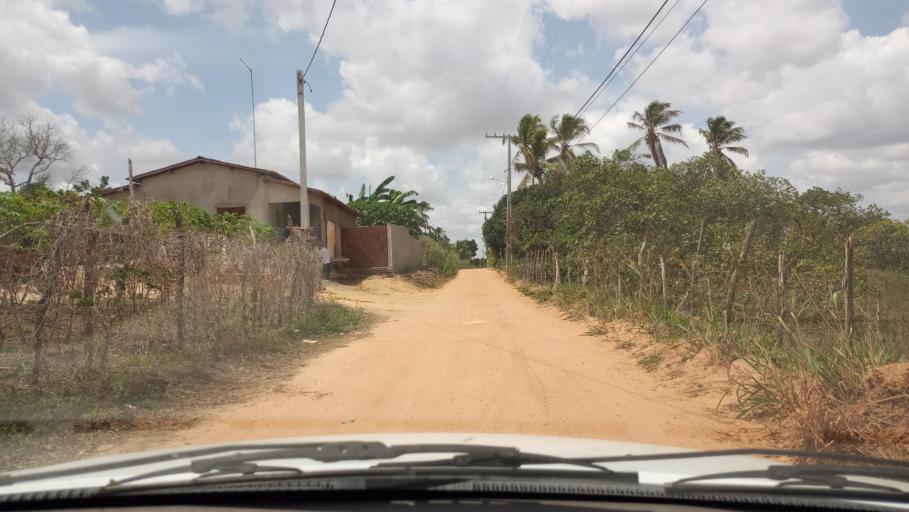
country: BR
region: Rio Grande do Norte
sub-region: Brejinho
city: Brejinho
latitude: -6.2594
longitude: -35.3402
